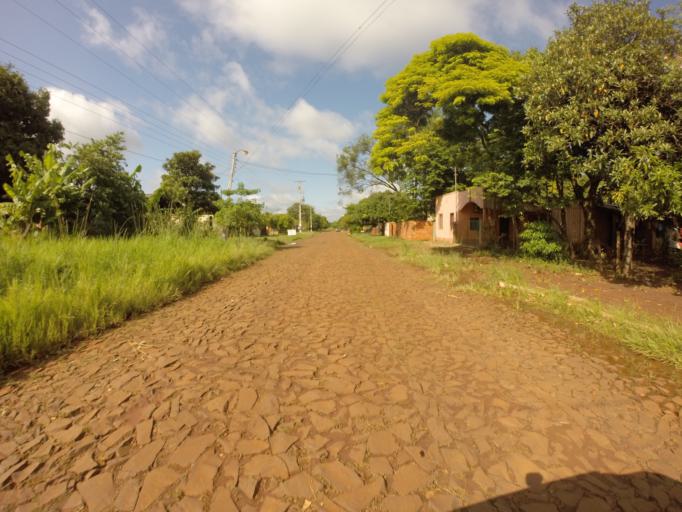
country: PY
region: Alto Parana
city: Ciudad del Este
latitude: -25.3973
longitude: -54.6474
